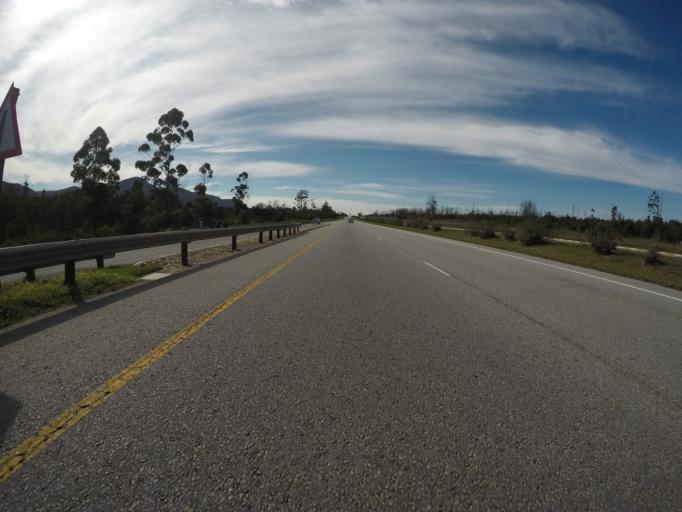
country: ZA
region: Eastern Cape
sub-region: Nelson Mandela Bay Metropolitan Municipality
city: Uitenhage
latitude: -33.9092
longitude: 25.2318
